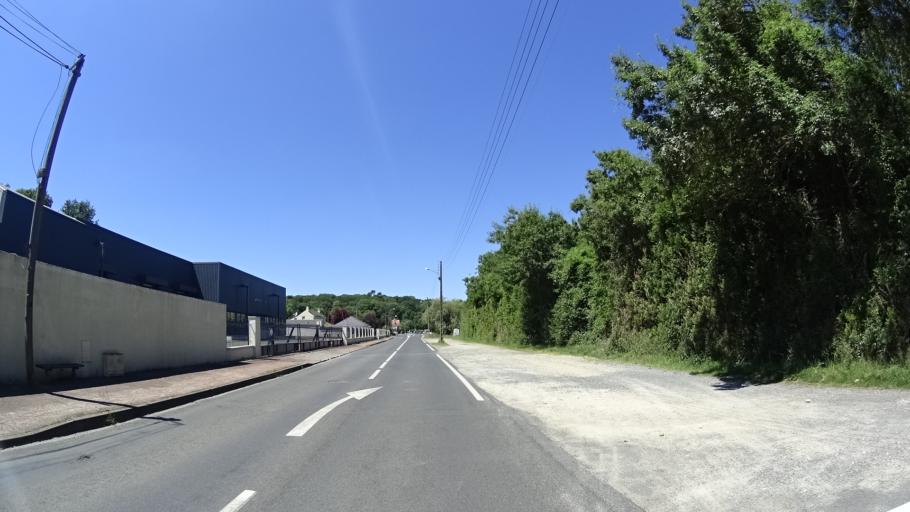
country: FR
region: Pays de la Loire
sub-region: Departement de Maine-et-Loire
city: Saumur
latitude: 47.2779
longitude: -0.1162
